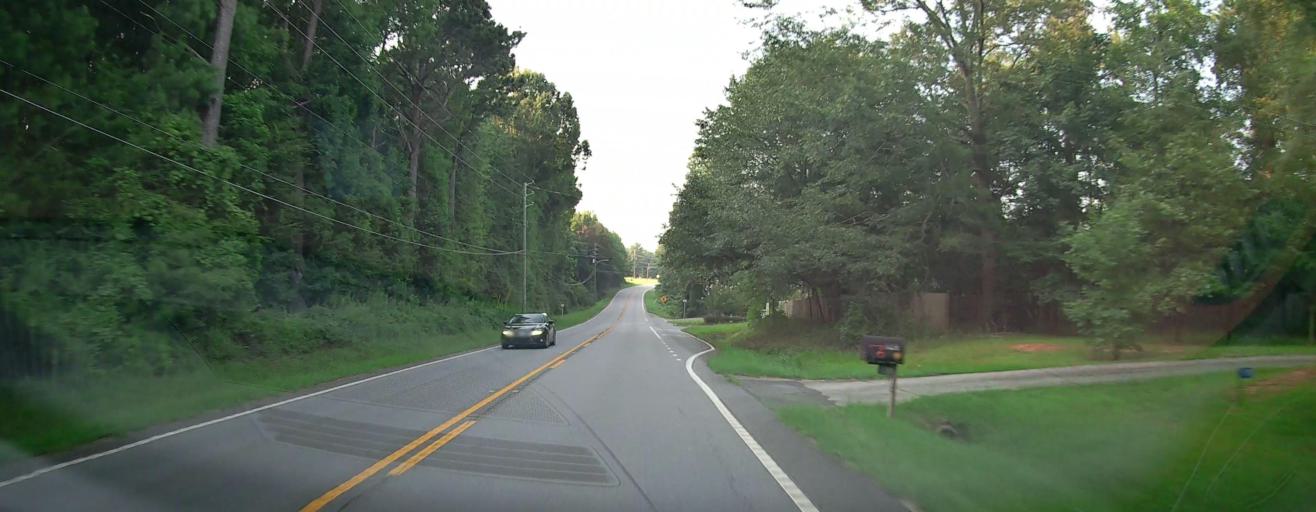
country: US
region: Georgia
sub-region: Jones County
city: Gray
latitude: 33.0161
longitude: -83.5323
